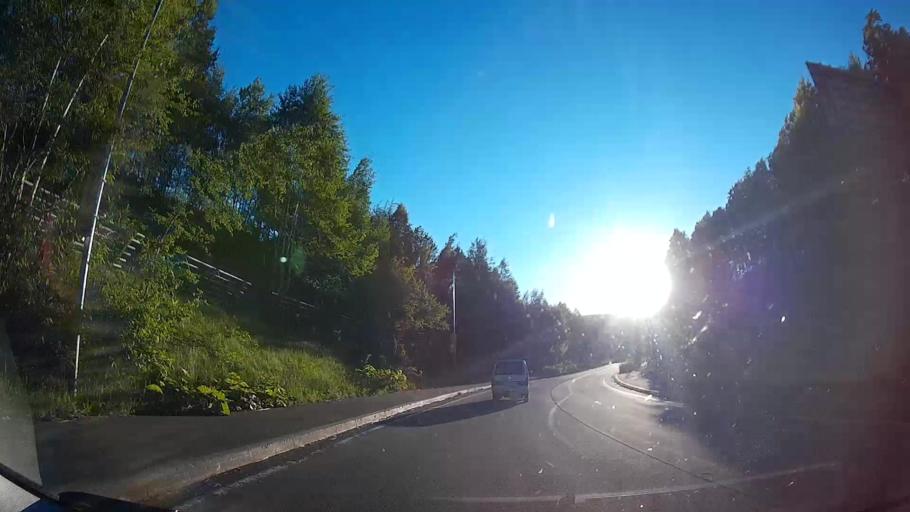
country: JP
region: Hokkaido
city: Otaru
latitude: 43.1630
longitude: 141.0272
